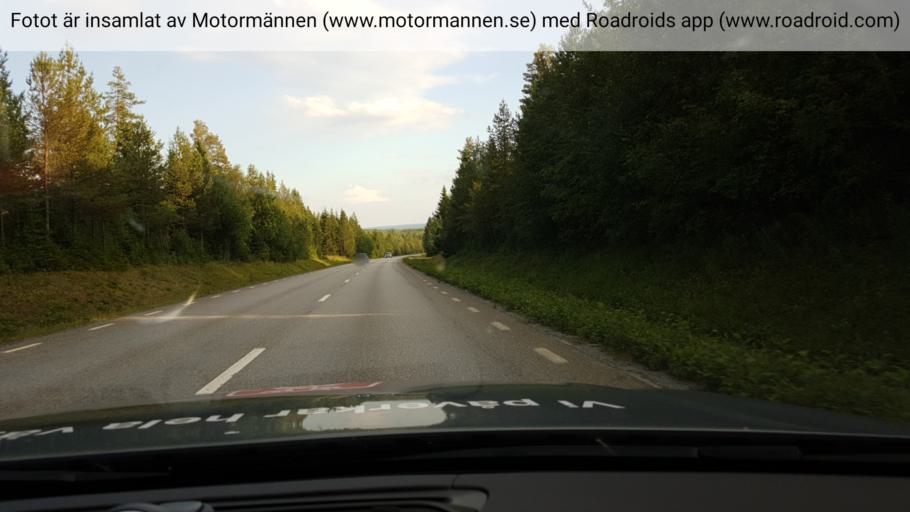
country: SE
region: Jaemtland
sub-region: Krokoms Kommun
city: Valla
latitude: 63.3005
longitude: 13.9264
